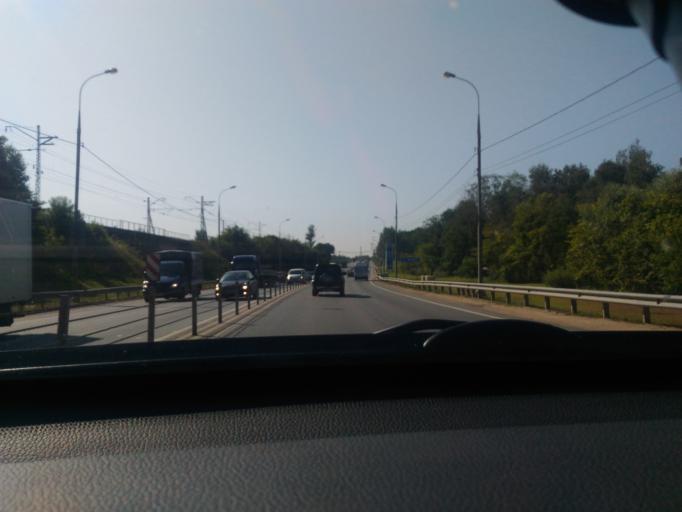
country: RU
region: Moskovskaya
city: Podosinki
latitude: 56.2000
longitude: 37.5246
